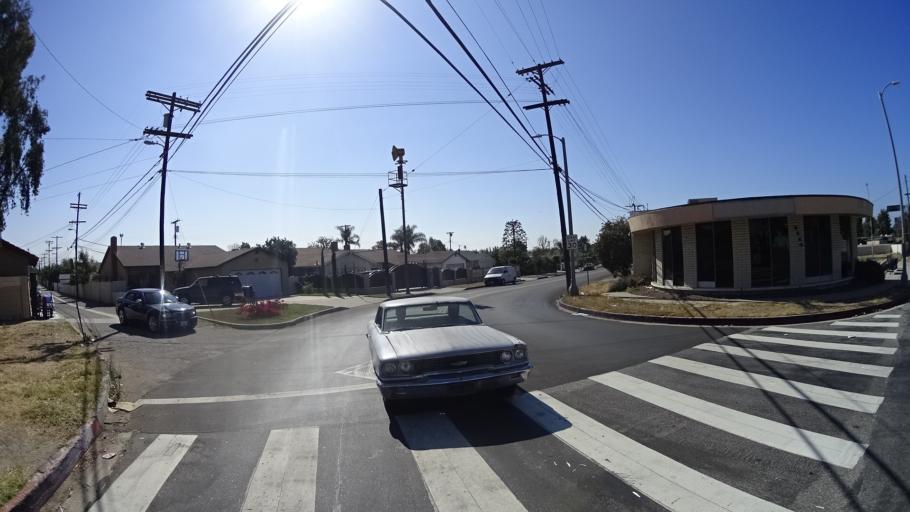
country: US
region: California
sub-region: Los Angeles County
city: Van Nuys
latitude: 34.2261
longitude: -118.4326
